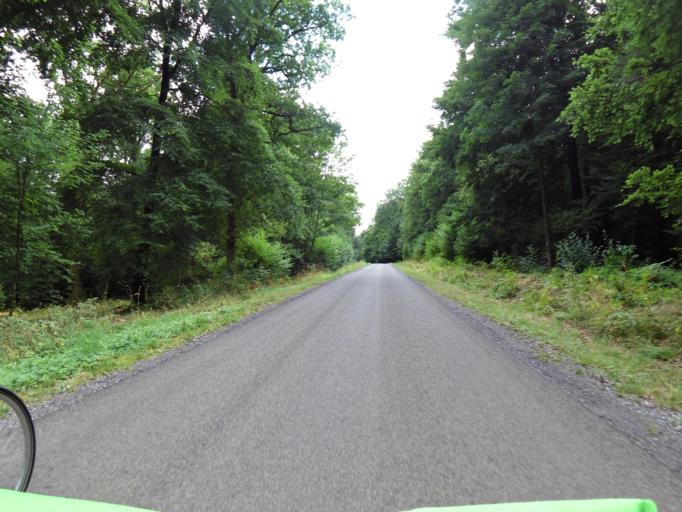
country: BE
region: Wallonia
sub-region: Province de Namur
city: Bievre
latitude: 49.9241
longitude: 5.0065
